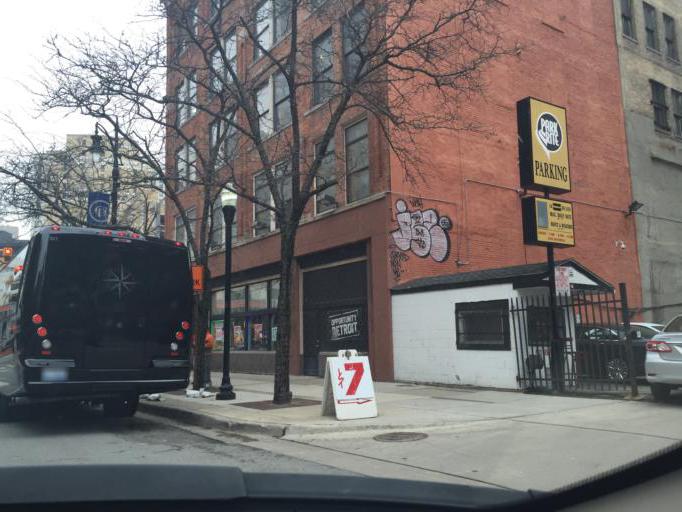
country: US
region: Michigan
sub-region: Wayne County
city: Detroit
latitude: 42.3334
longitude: -83.0495
